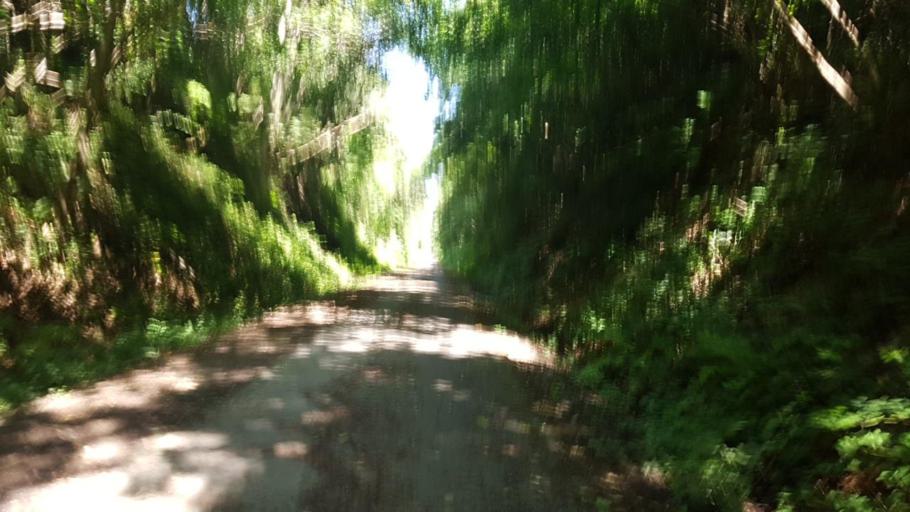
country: BE
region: Wallonia
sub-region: Province du Hainaut
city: Beaumont
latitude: 50.1972
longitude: 4.2268
